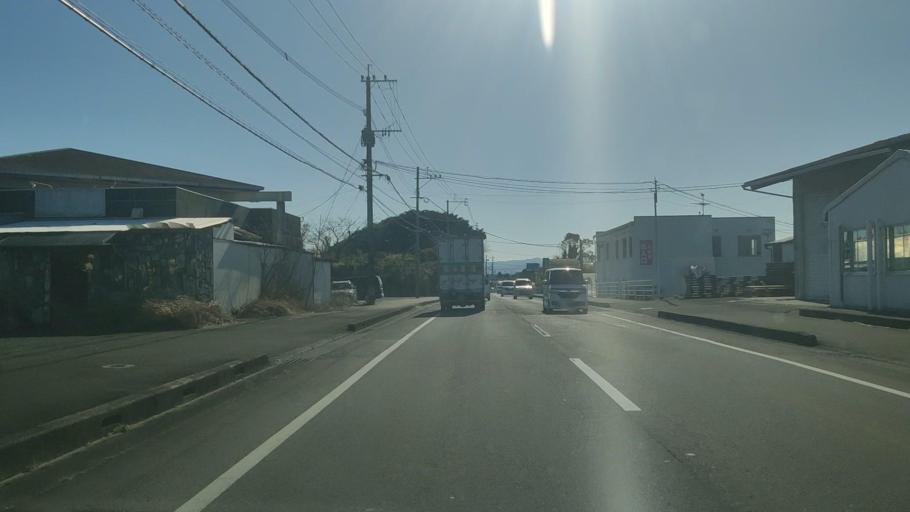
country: JP
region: Miyazaki
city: Miyazaki-shi
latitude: 31.9454
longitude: 131.4587
